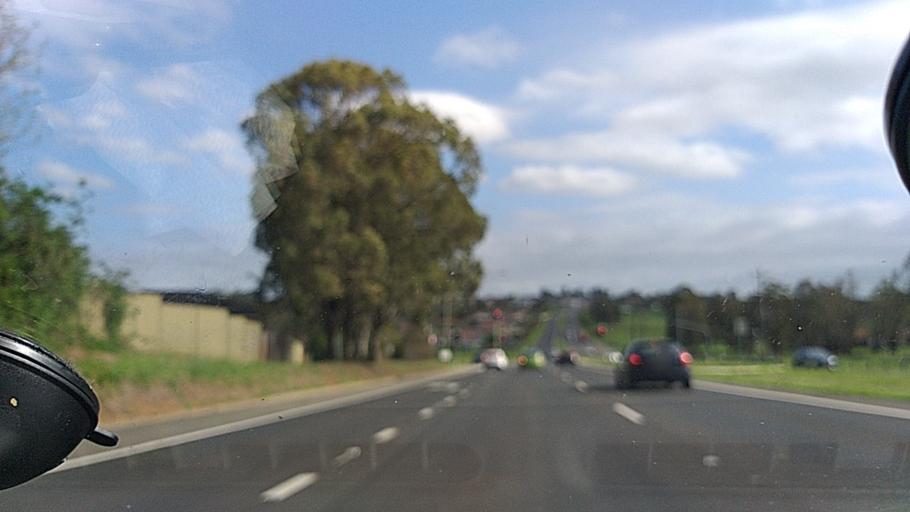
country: AU
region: New South Wales
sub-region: Campbelltown Municipality
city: Glen Alpine
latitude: -34.0938
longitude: 150.8051
